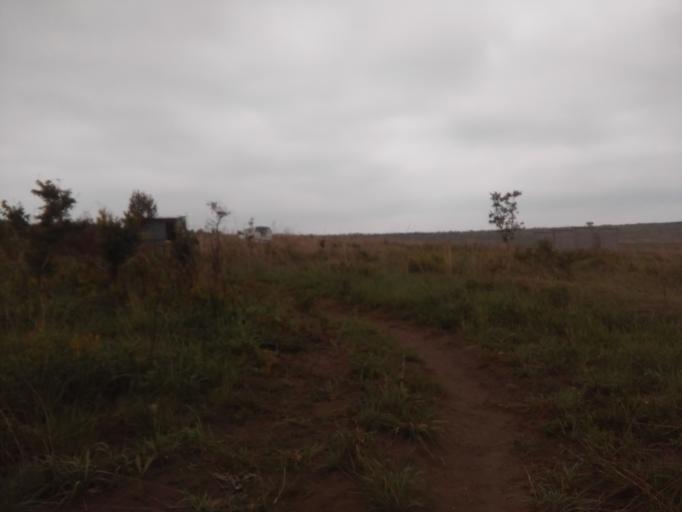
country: CD
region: Kinshasa
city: Masina
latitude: -4.4235
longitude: 15.9176
